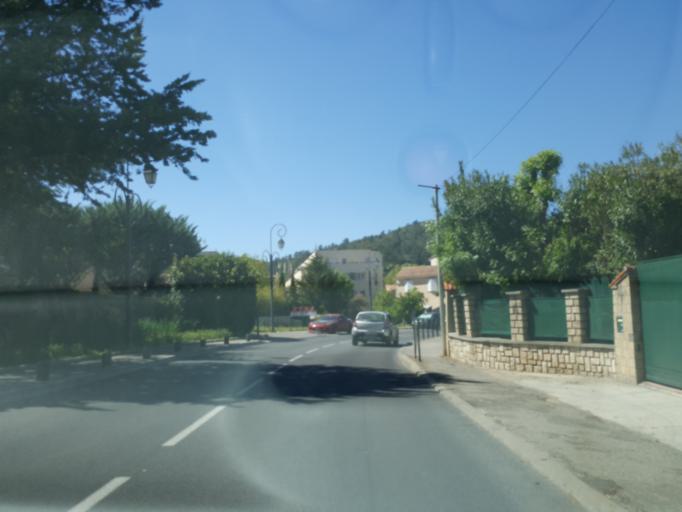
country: FR
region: Provence-Alpes-Cote d'Azur
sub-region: Departement des Bouches-du-Rhone
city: Auriol
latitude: 43.3685
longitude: 5.6378
